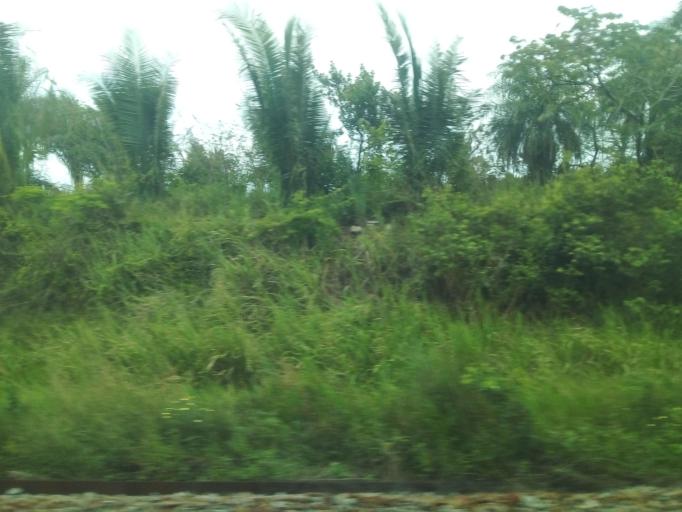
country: BR
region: Maranhao
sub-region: Arari
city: Arari
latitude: -3.5736
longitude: -44.7252
